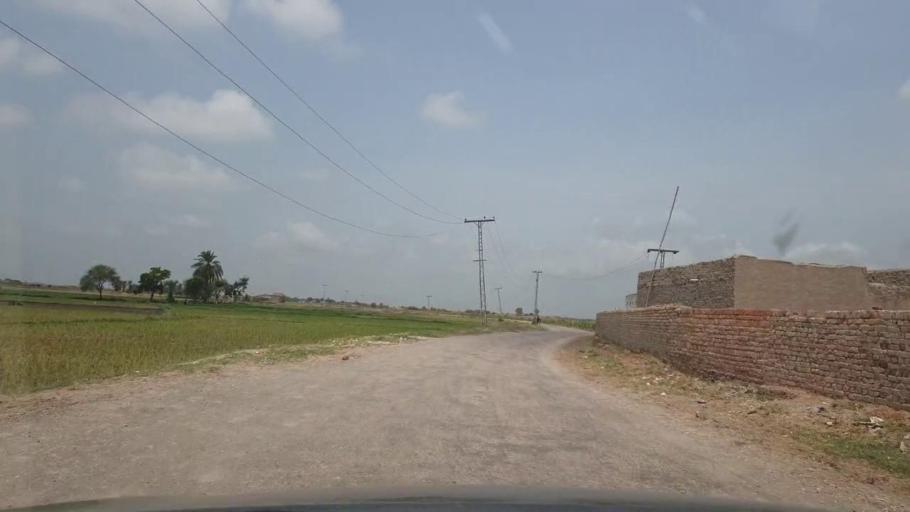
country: PK
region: Sindh
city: Ratodero
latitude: 27.9023
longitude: 68.3202
